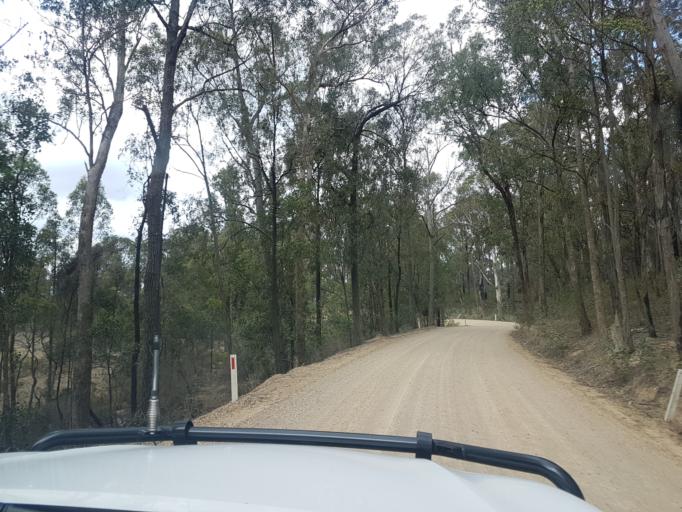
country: AU
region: Victoria
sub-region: East Gippsland
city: Bairnsdale
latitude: -37.6947
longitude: 147.5680
